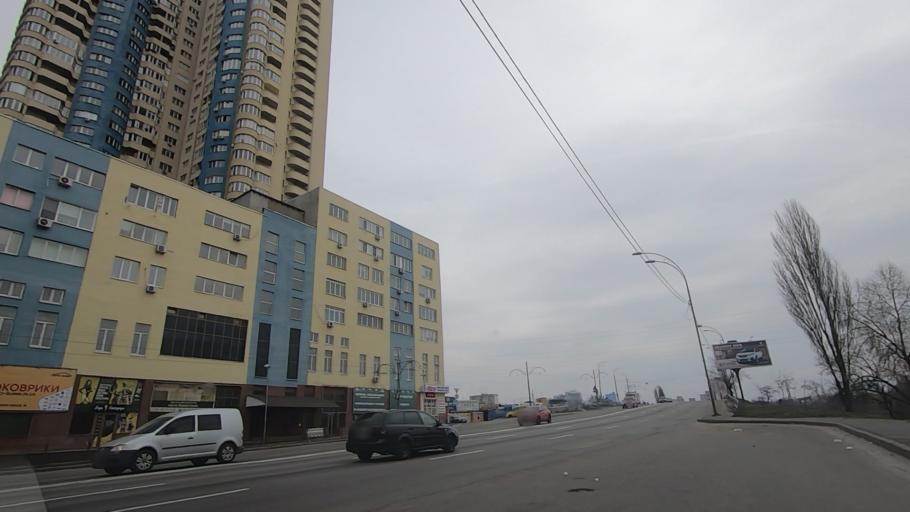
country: MD
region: Anenii Noi
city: Varnita
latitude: 46.9309
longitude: 29.4742
